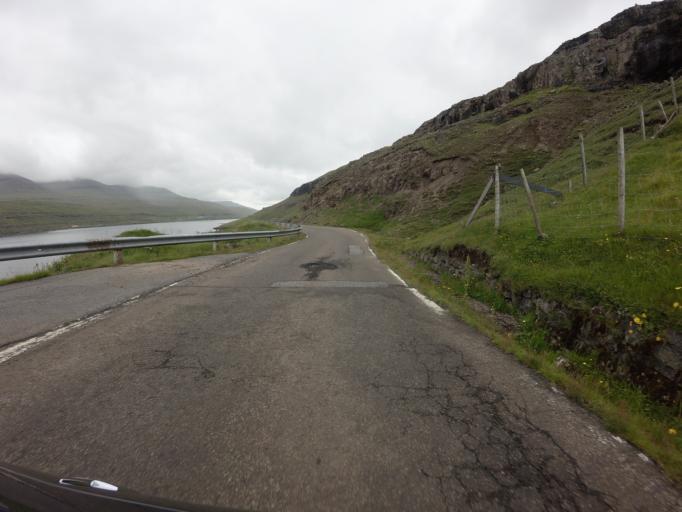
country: FO
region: Eysturoy
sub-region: Eidi
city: Eidi
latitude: 62.2877
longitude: -7.1044
